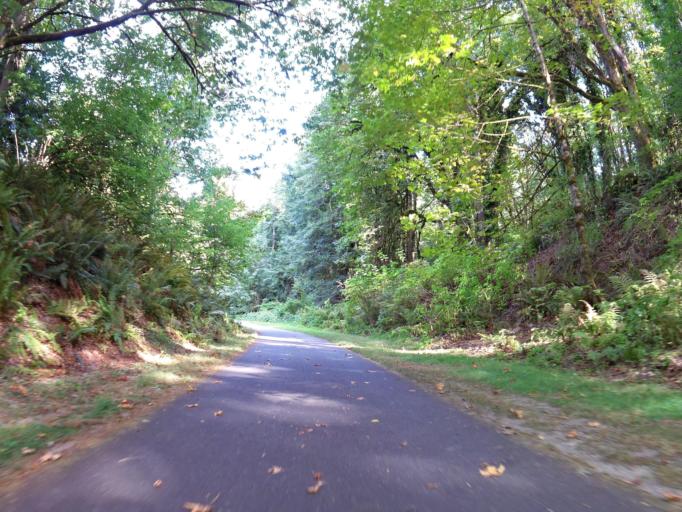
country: US
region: Washington
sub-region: Thurston County
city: Olympia
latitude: 47.0327
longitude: -122.8825
